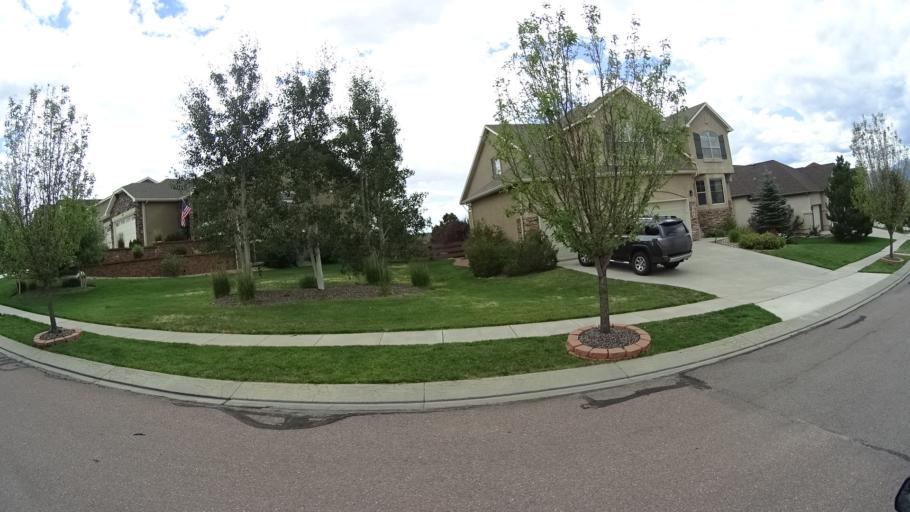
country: US
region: Colorado
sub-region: El Paso County
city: Gleneagle
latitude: 39.0307
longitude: -104.8127
